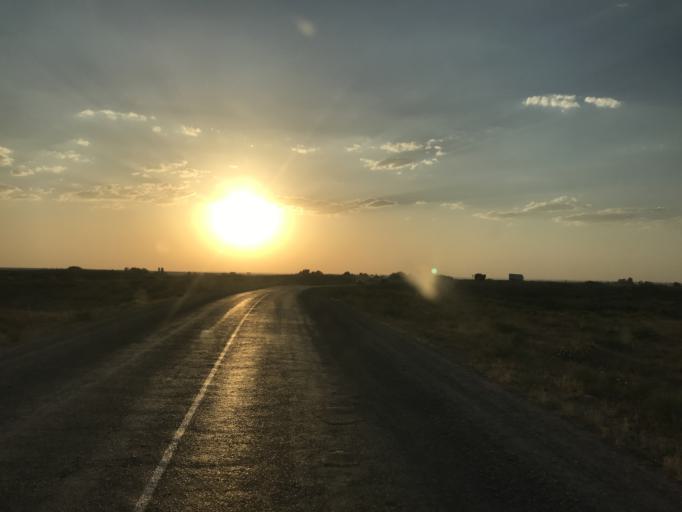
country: UZ
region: Toshkent
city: Yangiyul
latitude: 41.3376
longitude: 68.8812
